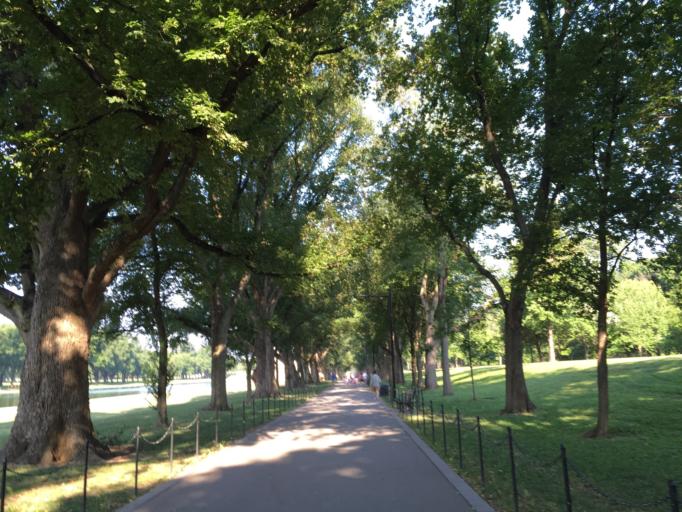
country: US
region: Washington, D.C.
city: Washington, D.C.
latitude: 38.8899
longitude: -77.0429
